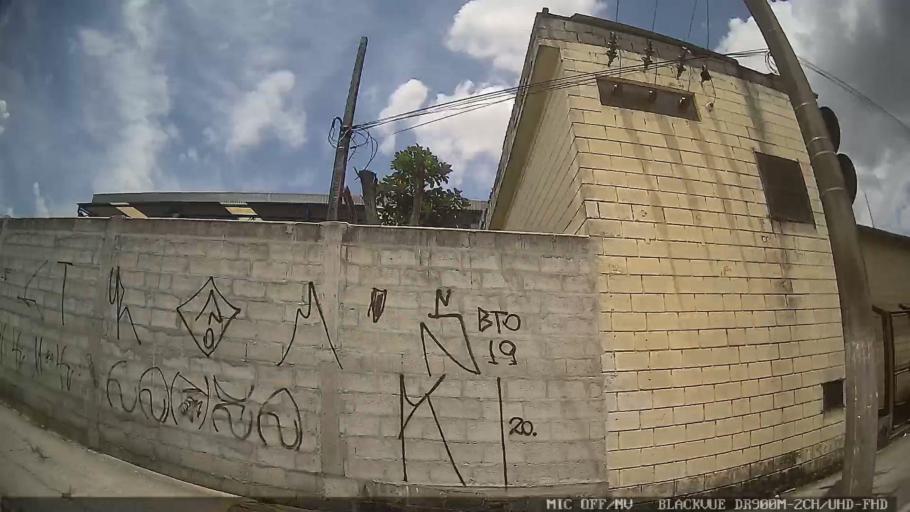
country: BR
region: Sao Paulo
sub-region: Mogi das Cruzes
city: Mogi das Cruzes
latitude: -23.5318
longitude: -46.2198
